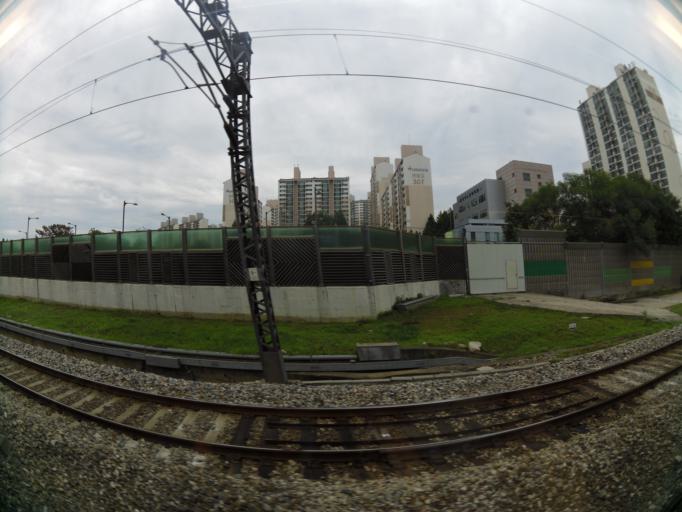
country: KR
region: Gyeonggi-do
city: Anyang-si
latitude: 37.3450
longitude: 126.9483
